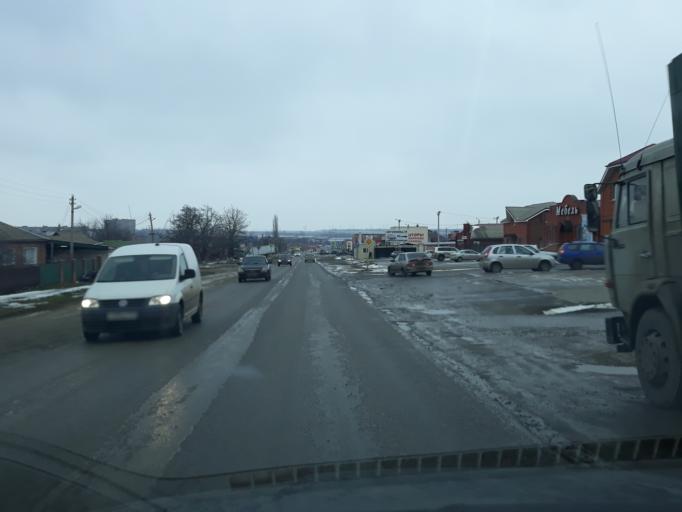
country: RU
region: Rostov
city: Krym
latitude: 47.2805
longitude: 39.5158
